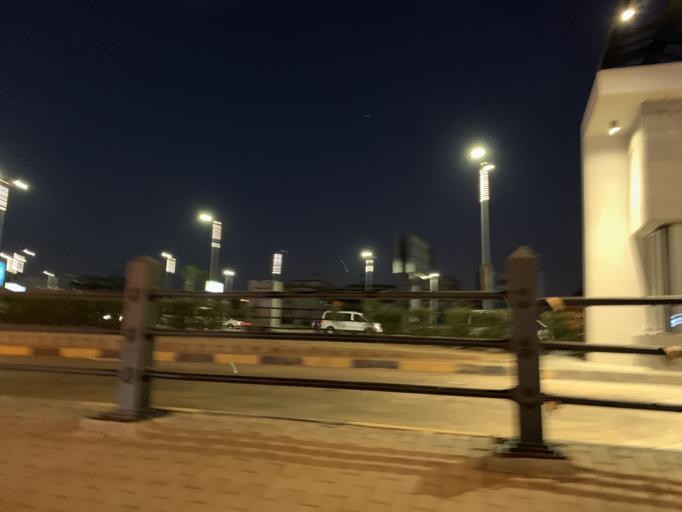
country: EG
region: Al Jizah
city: Awsim
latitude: 30.0051
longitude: 30.9753
